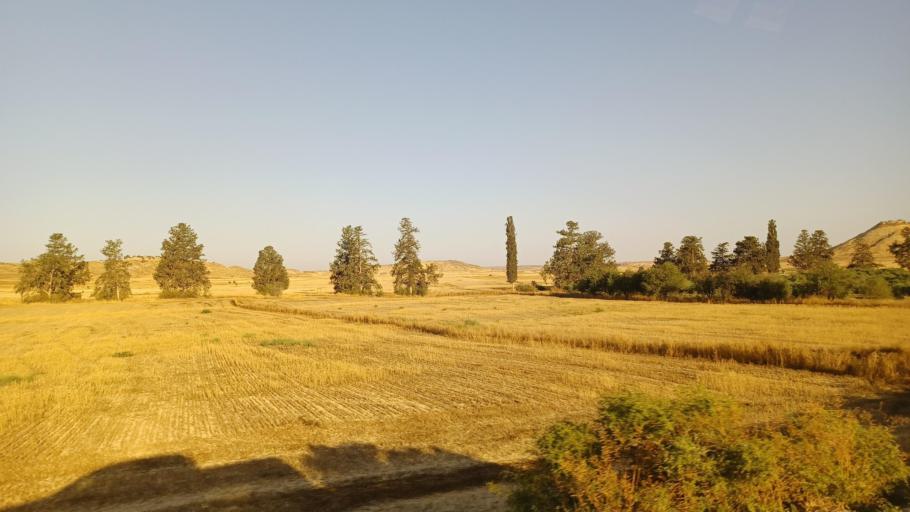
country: CY
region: Larnaka
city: Athienou
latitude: 35.0545
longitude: 33.4987
